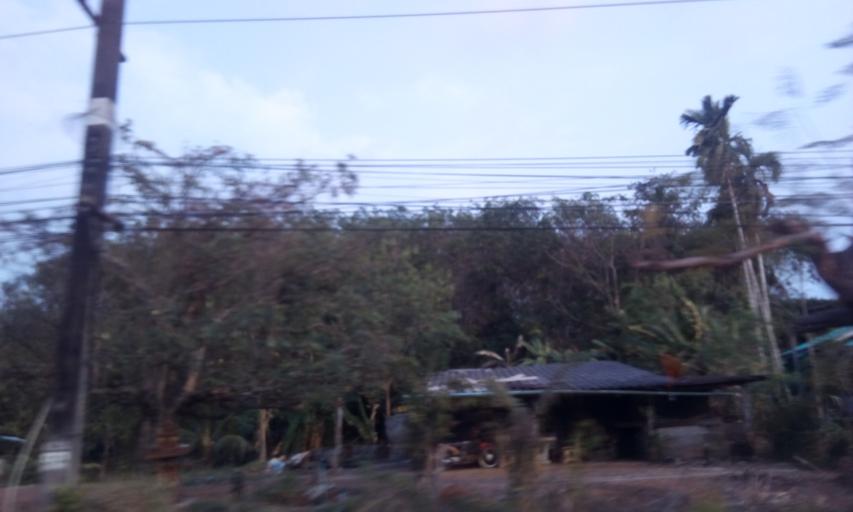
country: TH
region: Trat
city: Khao Saming
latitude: 12.2963
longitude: 102.3341
